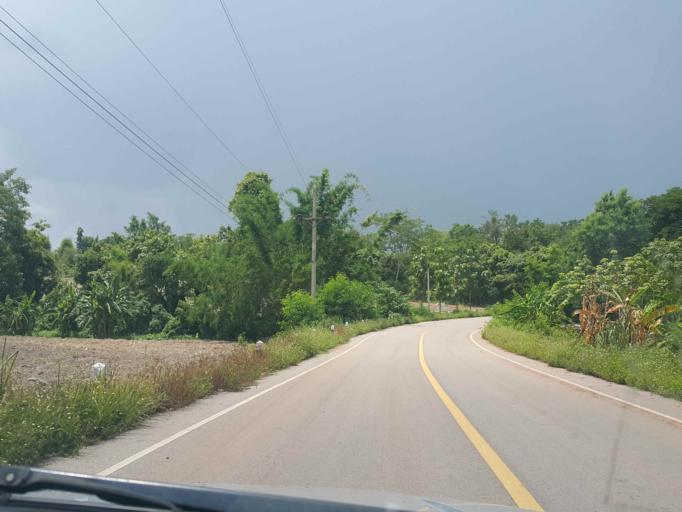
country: TH
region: Phayao
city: Dok Kham Tai
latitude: 19.0504
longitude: 99.9501
